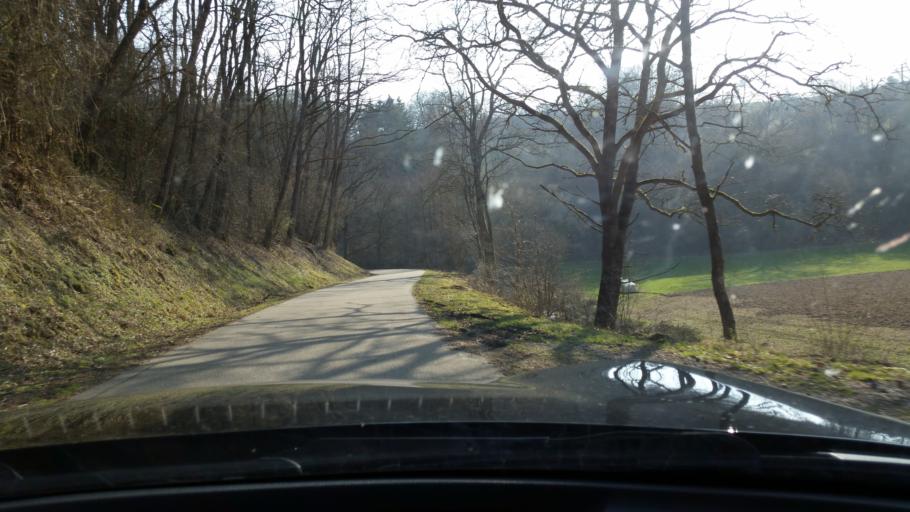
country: DE
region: Baden-Wuerttemberg
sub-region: Regierungsbezirk Stuttgart
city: Mockmuhl
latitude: 49.3357
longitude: 9.3858
